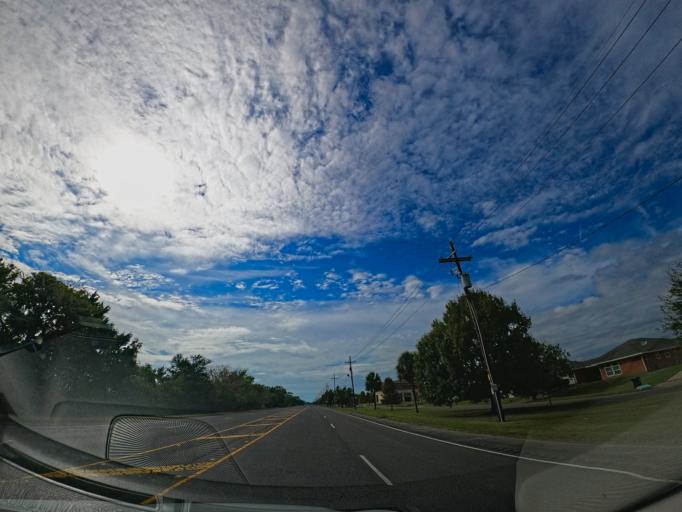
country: US
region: Louisiana
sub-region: Saint Tammany Parish
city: Eden Isle
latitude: 30.0647
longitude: -89.8120
